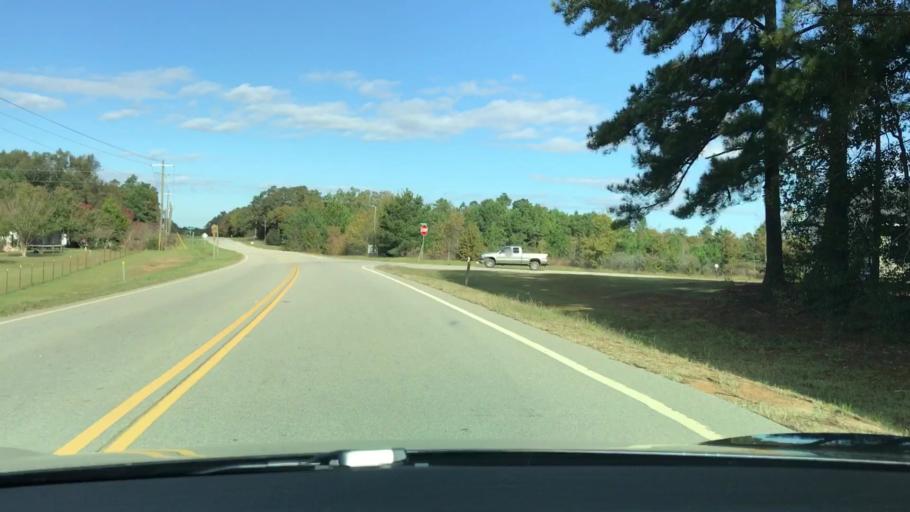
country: US
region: Georgia
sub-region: Jefferson County
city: Wrens
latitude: 33.1877
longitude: -82.4556
